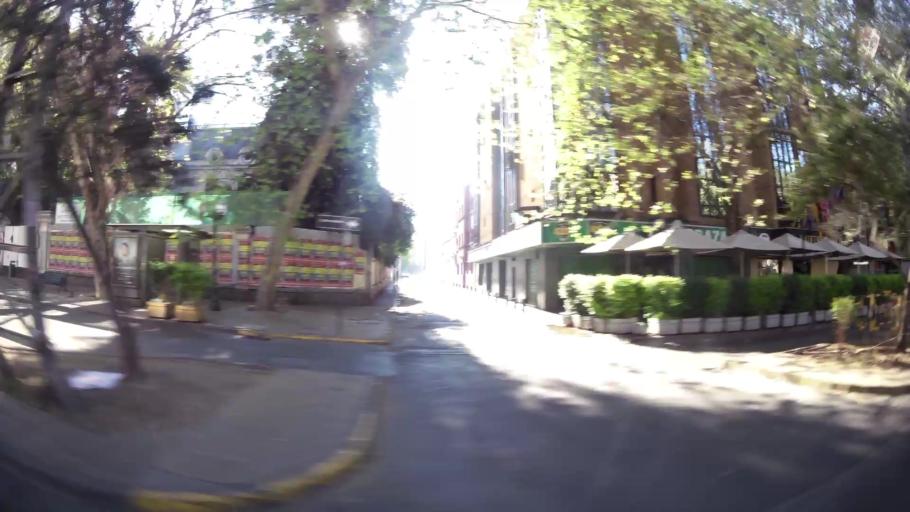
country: CL
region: Santiago Metropolitan
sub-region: Provincia de Santiago
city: Santiago
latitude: -33.4386
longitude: -70.6348
